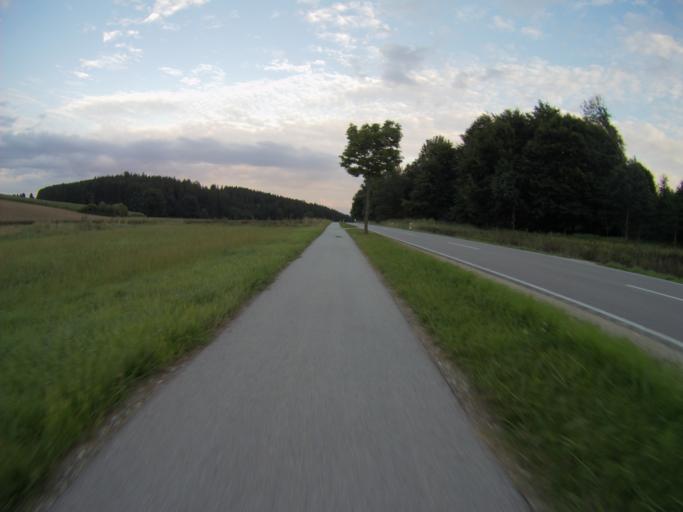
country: DE
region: Bavaria
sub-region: Upper Bavaria
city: Kirchdorf
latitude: 48.4325
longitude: 11.6927
